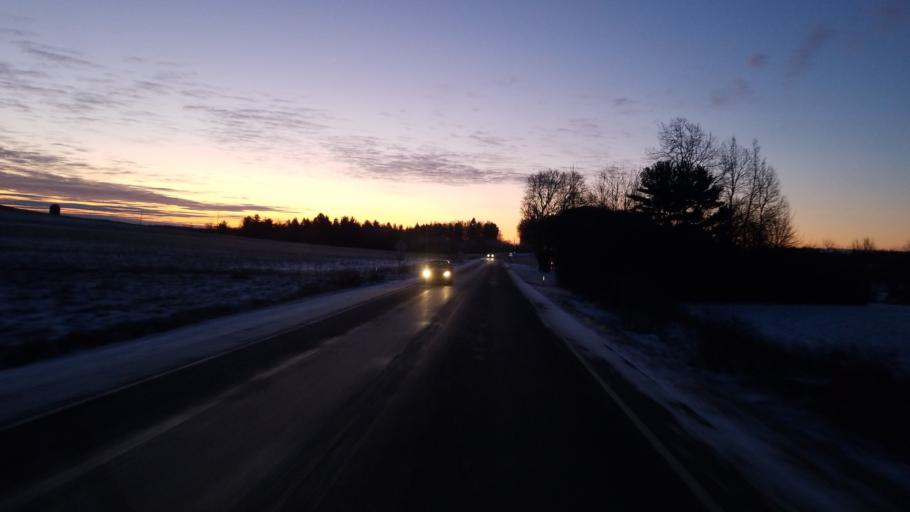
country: US
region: Pennsylvania
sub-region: Clarion County
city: Knox
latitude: 41.2584
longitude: -79.5547
